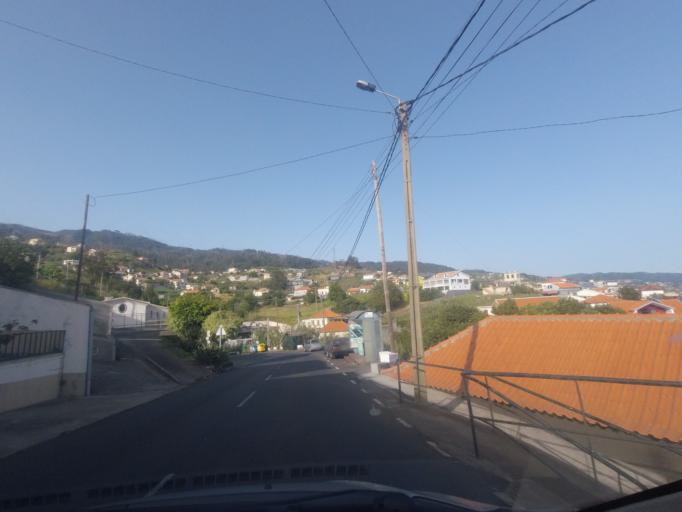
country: PT
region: Madeira
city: Ponta do Sol
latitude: 32.6989
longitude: -17.1142
